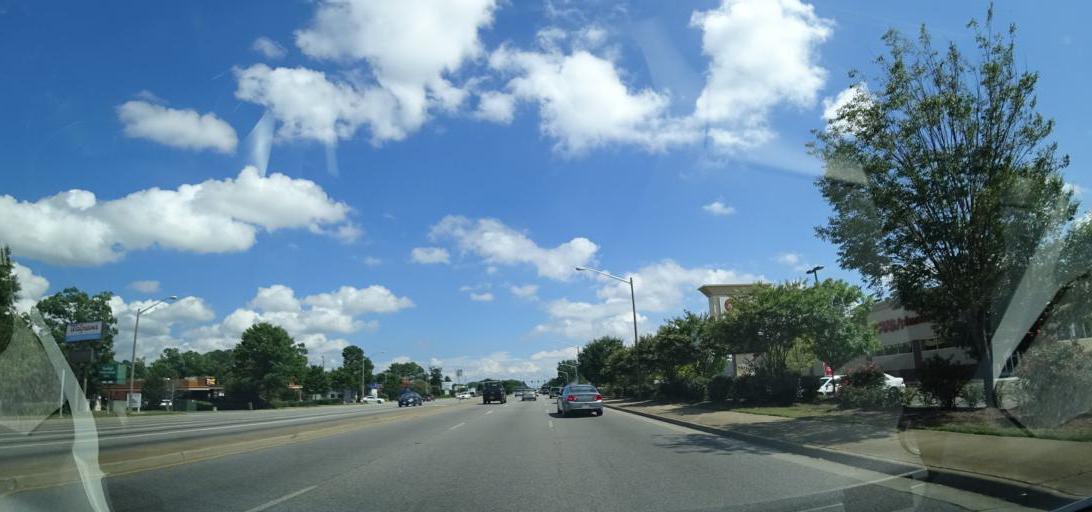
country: US
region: Virginia
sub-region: York County
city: Yorktown
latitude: 37.1384
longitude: -76.5199
